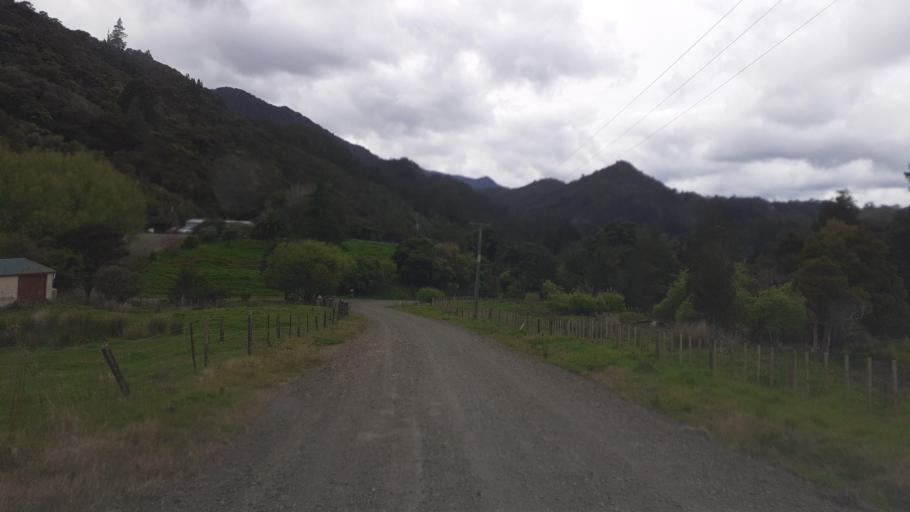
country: NZ
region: Northland
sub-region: Far North District
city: Kaitaia
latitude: -35.5312
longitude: 173.4316
